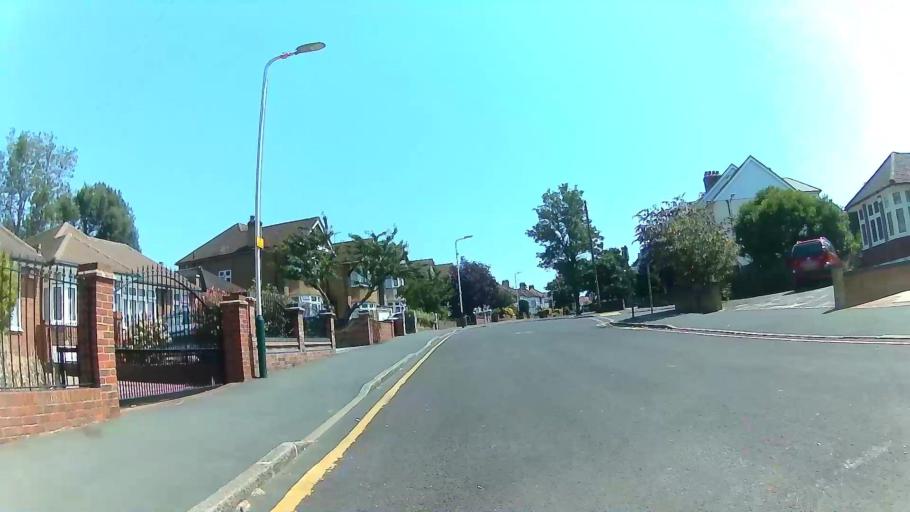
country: GB
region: England
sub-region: Greater London
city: Upminster
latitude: 51.5533
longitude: 0.2382
